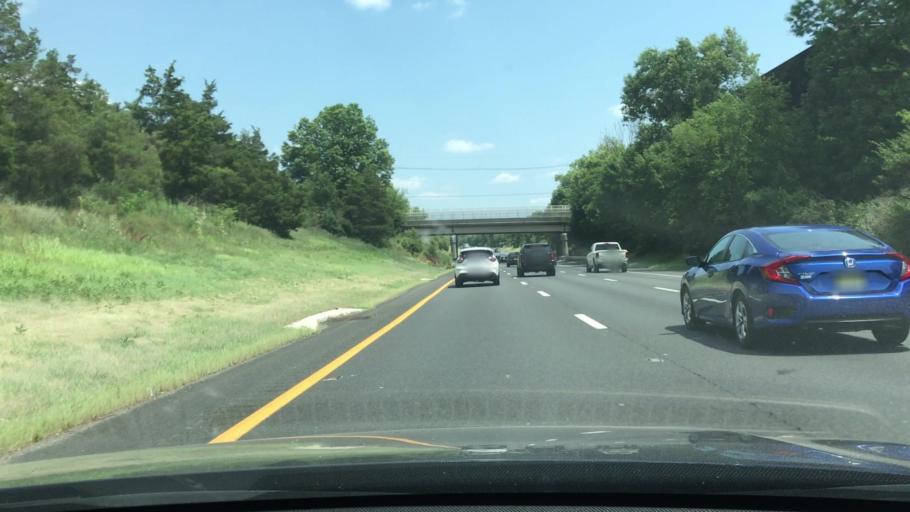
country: US
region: New Jersey
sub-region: Somerset County
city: Somerville
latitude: 40.5818
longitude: -74.5998
